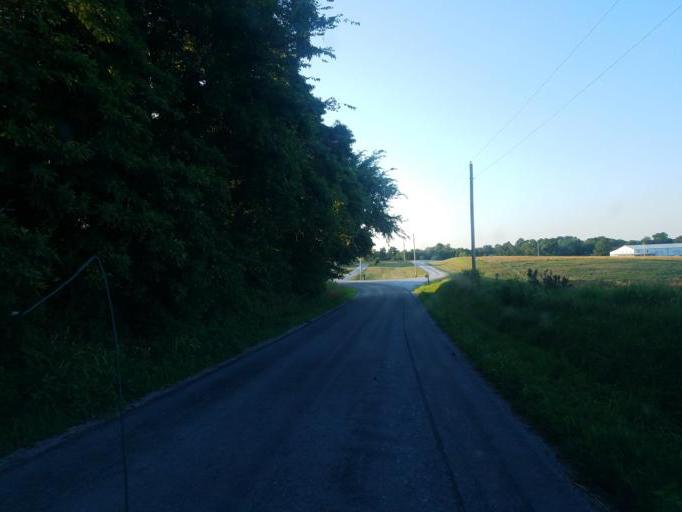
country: US
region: Illinois
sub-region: Jackson County
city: Murphysboro
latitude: 37.6768
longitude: -89.3092
